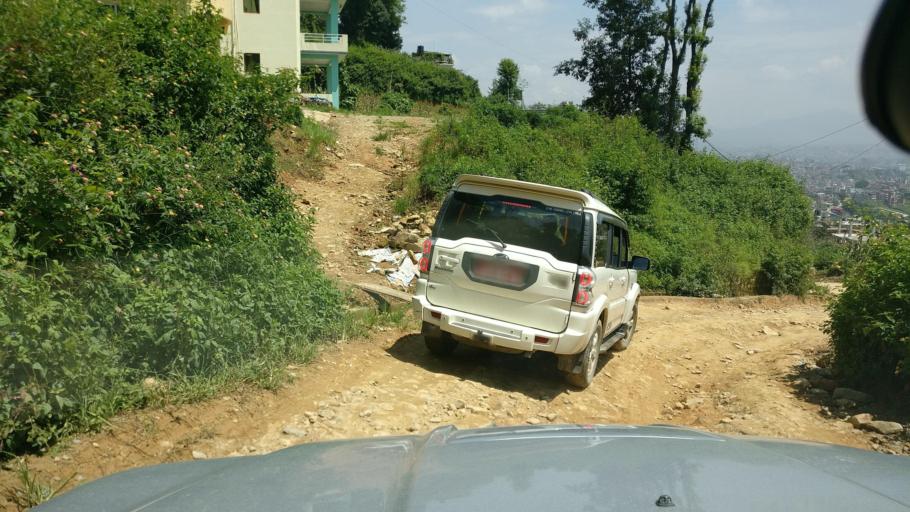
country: NP
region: Central Region
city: Kirtipur
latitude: 27.7029
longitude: 85.2570
